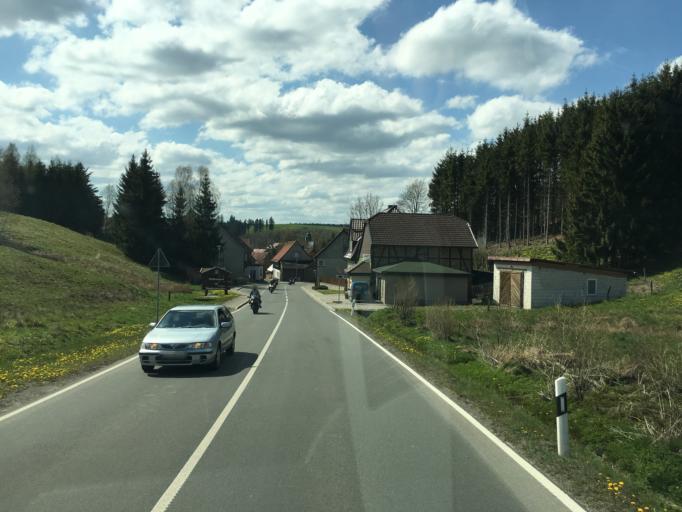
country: DE
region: Saxony-Anhalt
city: Hasselfelde
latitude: 51.6850
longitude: 10.7910
